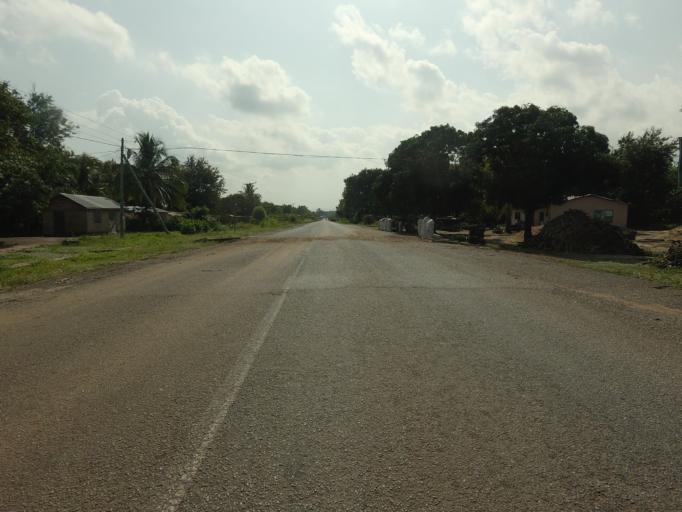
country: GH
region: Volta
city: Ho
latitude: 6.5740
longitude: 0.5931
